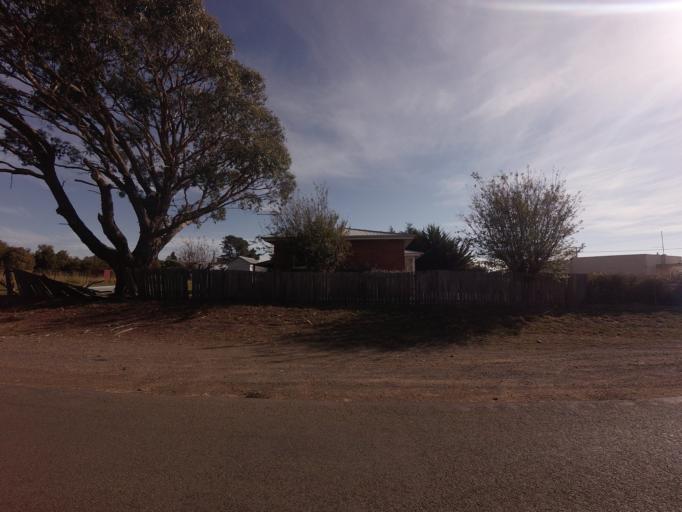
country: AU
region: Tasmania
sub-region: Sorell
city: Sorell
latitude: -42.4538
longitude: 147.4616
